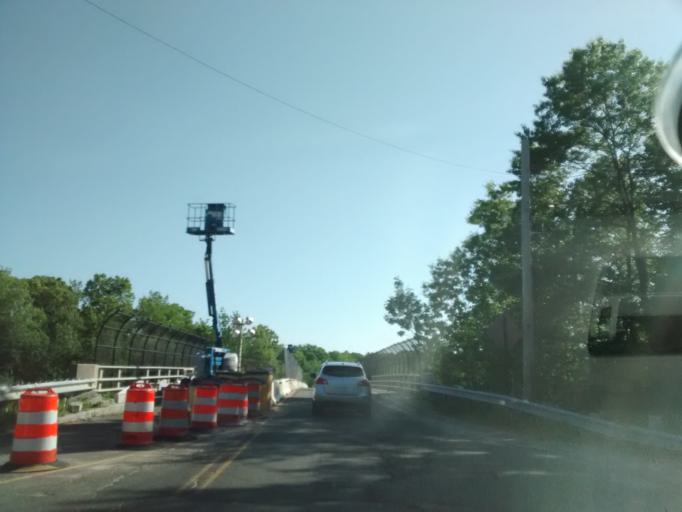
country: US
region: Massachusetts
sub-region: Worcester County
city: Charlton
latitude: 42.1537
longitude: -71.9777
